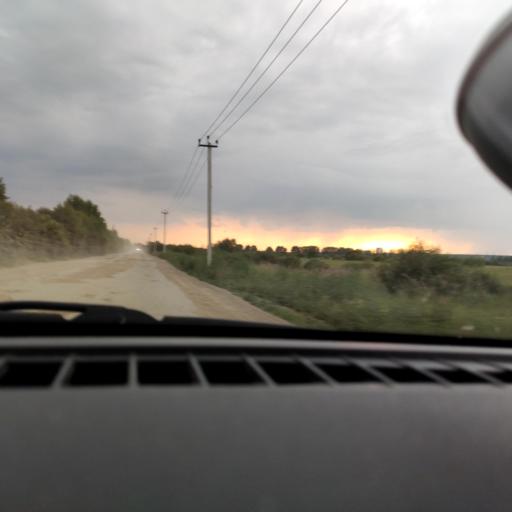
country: RU
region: Perm
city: Kondratovo
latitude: 58.0049
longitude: 56.0292
